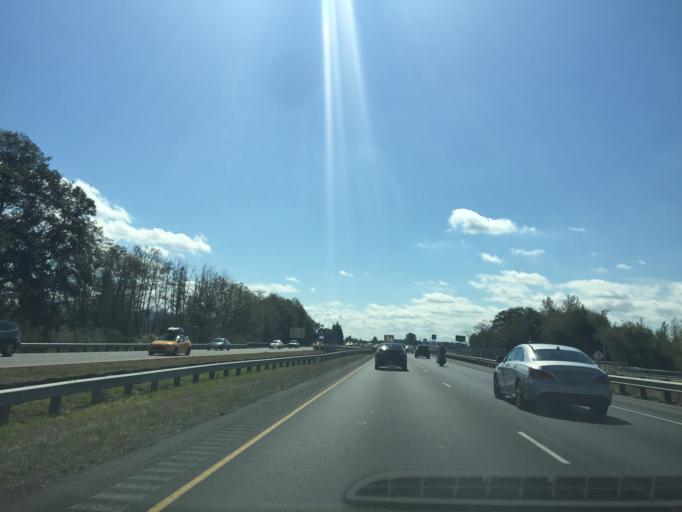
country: US
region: Washington
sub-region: Skagit County
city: Burlington
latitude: 48.4601
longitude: -122.3417
